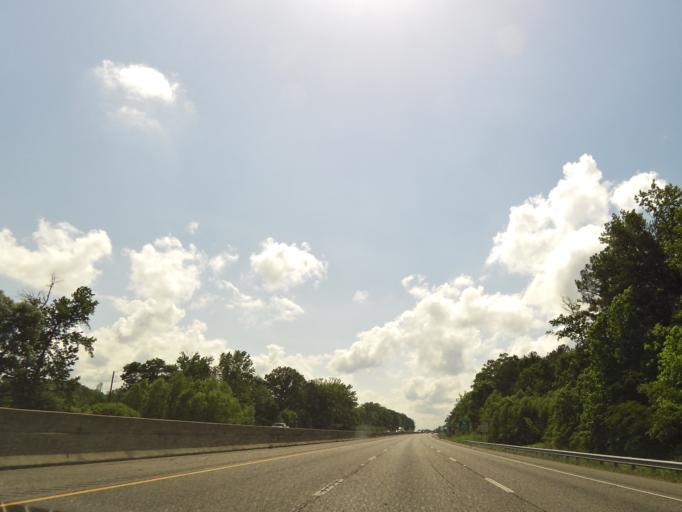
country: US
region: Alabama
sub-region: Saint Clair County
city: Pell City
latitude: 33.6069
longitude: -86.2660
